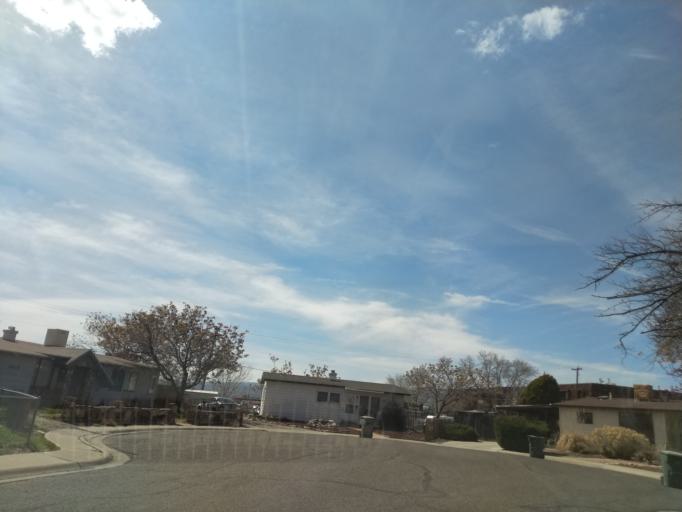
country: US
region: Colorado
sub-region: Mesa County
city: Grand Junction
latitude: 39.0798
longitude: -108.5350
